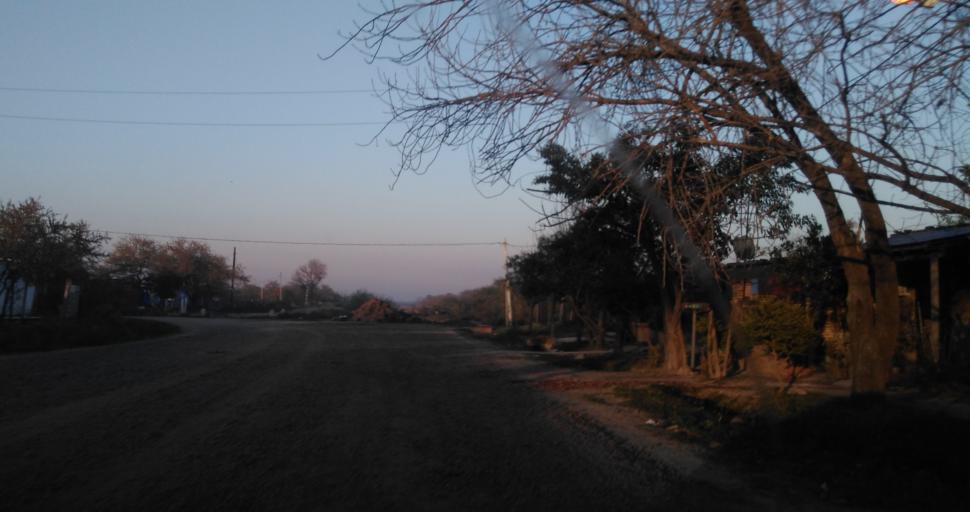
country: AR
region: Chaco
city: Resistencia
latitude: -27.4889
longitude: -59.0003
